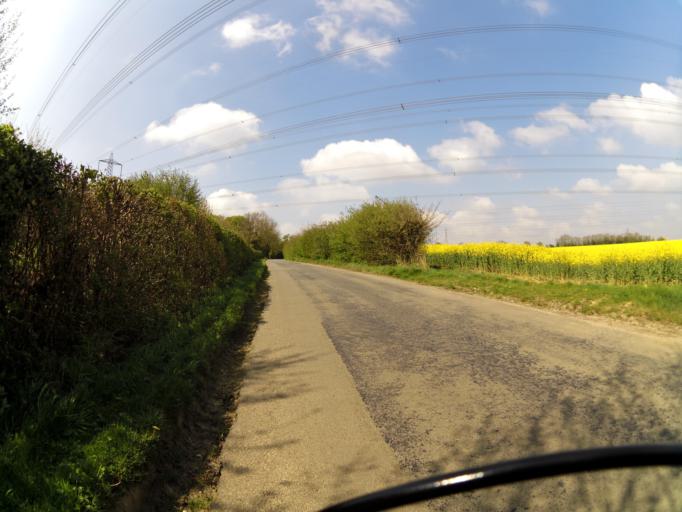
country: GB
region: England
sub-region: Suffolk
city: Bramford
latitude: 52.0820
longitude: 1.0713
